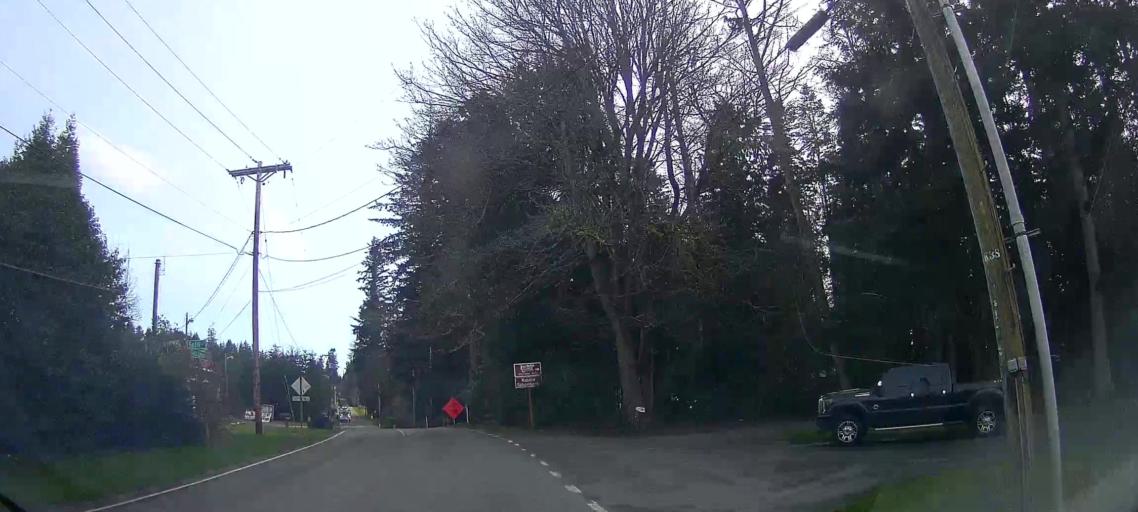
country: US
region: Washington
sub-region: Island County
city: Langley
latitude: 48.0939
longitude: -122.4110
